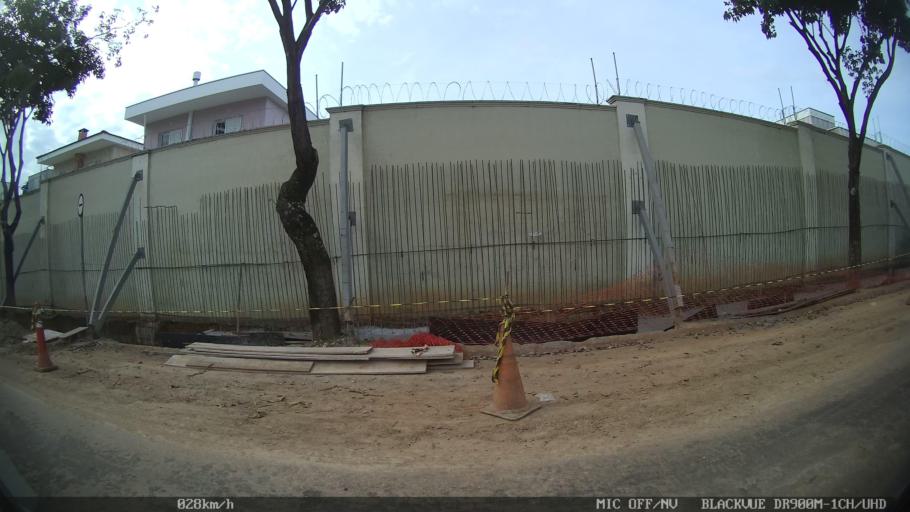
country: BR
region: Sao Paulo
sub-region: Piracicaba
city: Piracicaba
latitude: -22.7482
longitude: -47.6172
